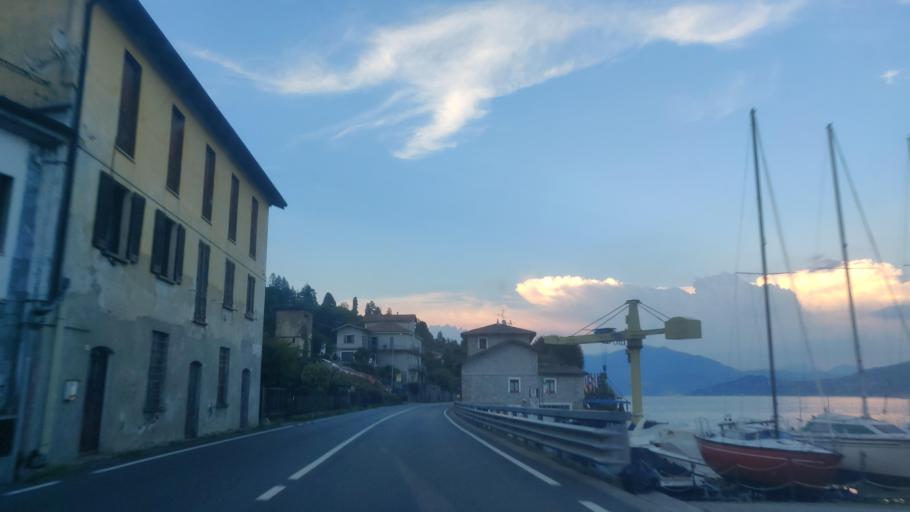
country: IT
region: Piedmont
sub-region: Provincia Verbano-Cusio-Ossola
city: Ghiffa
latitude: 45.9506
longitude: 8.6066
